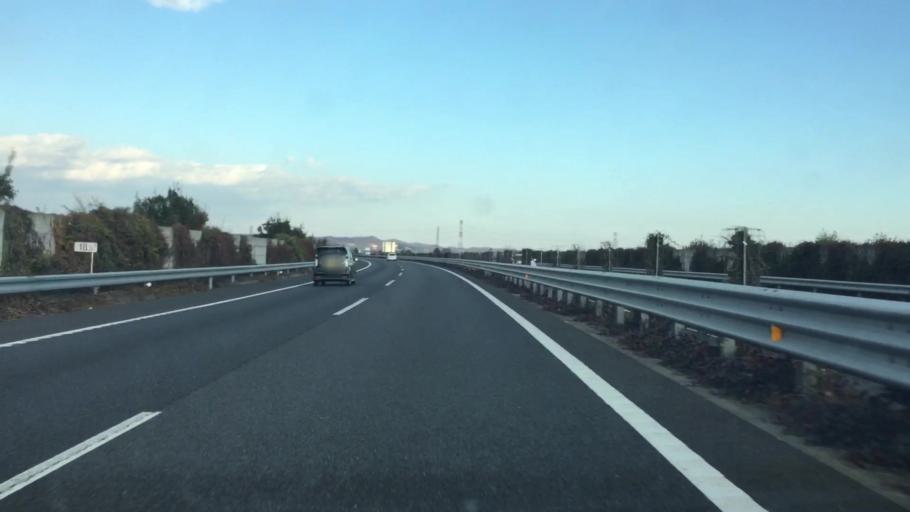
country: JP
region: Gunma
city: Isesaki
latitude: 36.3440
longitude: 139.2601
